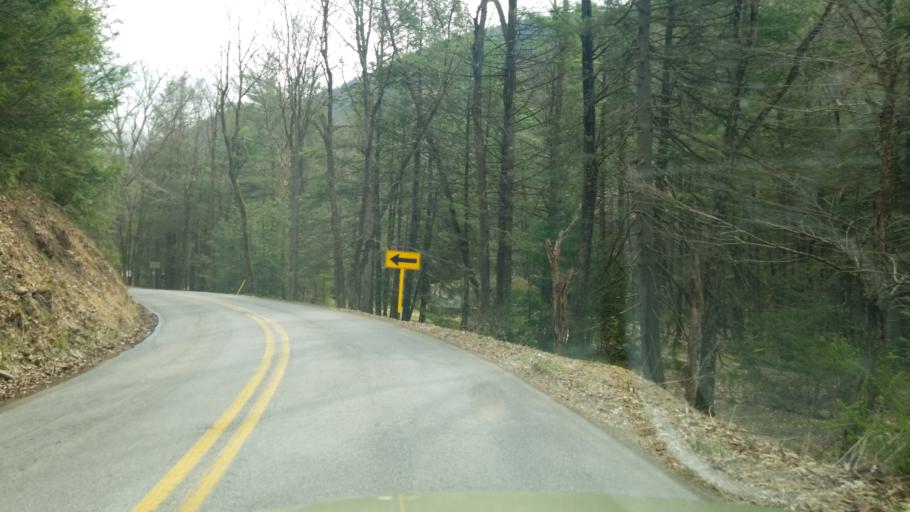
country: US
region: Pennsylvania
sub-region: Cameron County
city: Emporium
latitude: 41.2951
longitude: -78.1139
